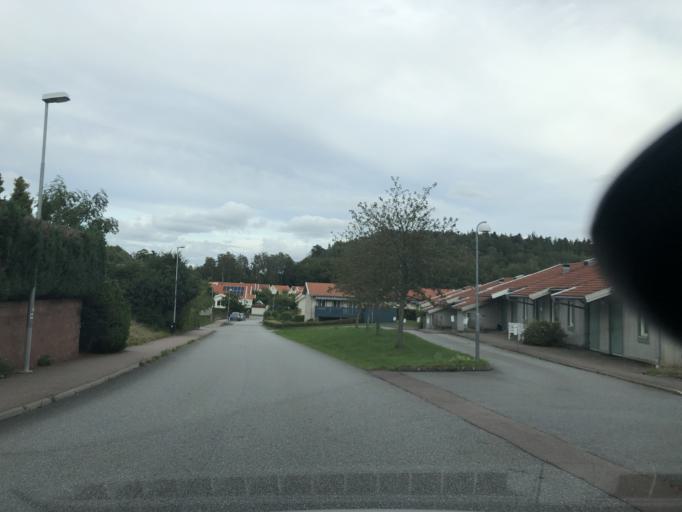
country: SE
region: Vaestra Goetaland
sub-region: Goteborg
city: Goeteborg
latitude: 57.7531
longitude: 11.9596
